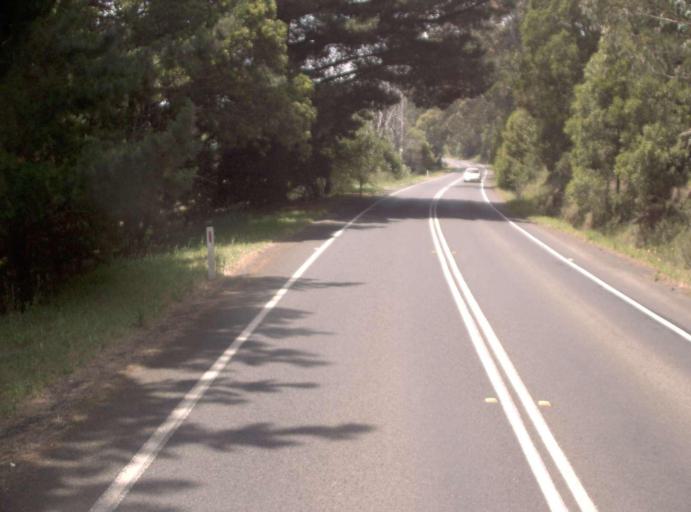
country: AU
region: Victoria
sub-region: Latrobe
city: Traralgon
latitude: -38.3599
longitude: 146.7396
